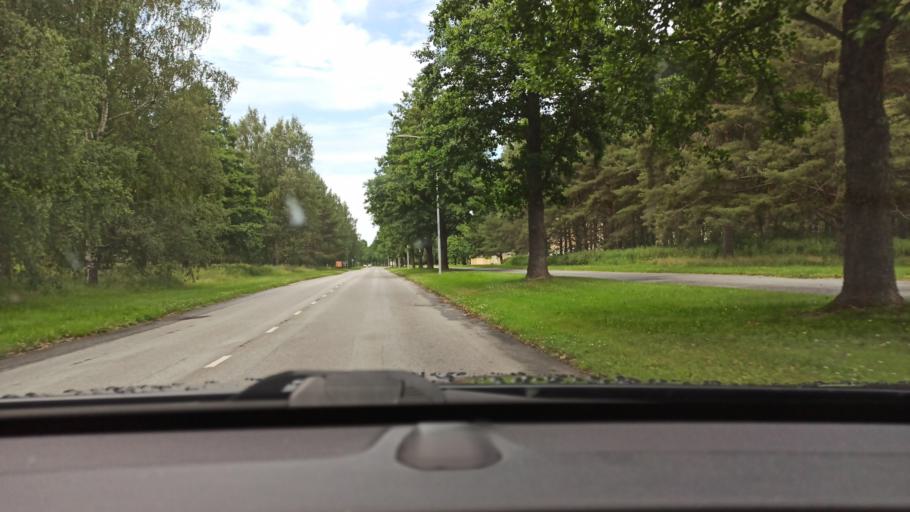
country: FI
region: Satakunta
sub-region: Pori
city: Pori
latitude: 61.5005
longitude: 21.7841
